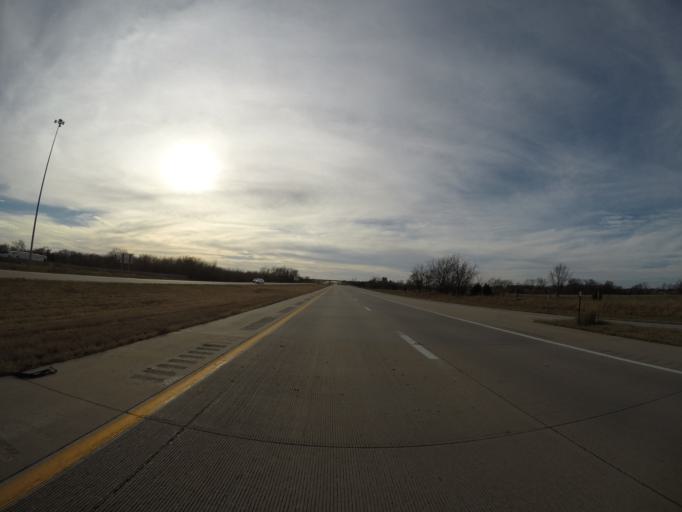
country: US
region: Kansas
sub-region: Franklin County
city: Wellsville
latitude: 38.7036
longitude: -95.0785
